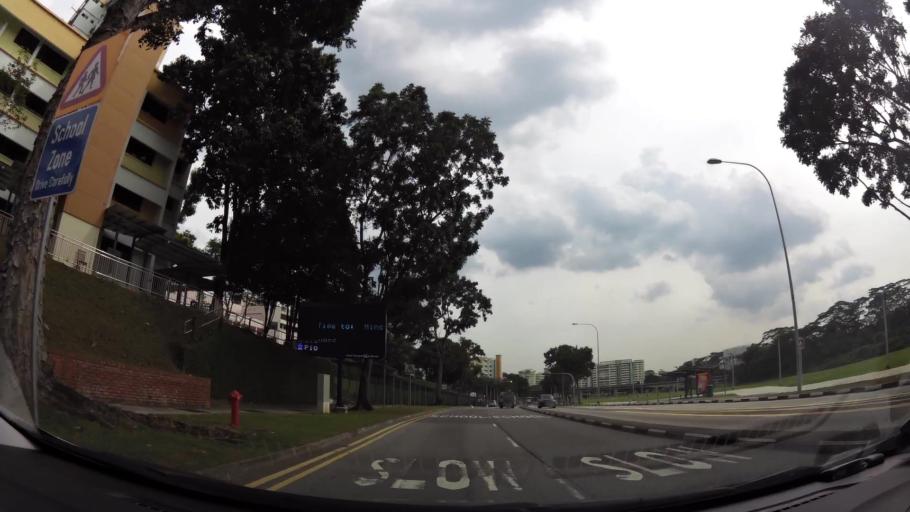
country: MY
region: Johor
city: Johor Bahru
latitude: 1.4358
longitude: 103.7722
